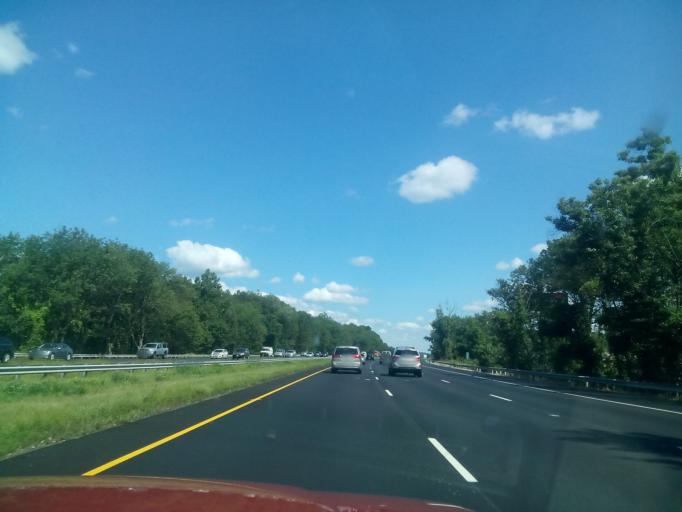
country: US
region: New Jersey
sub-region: Morris County
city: Wharton
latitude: 40.9088
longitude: -74.5924
